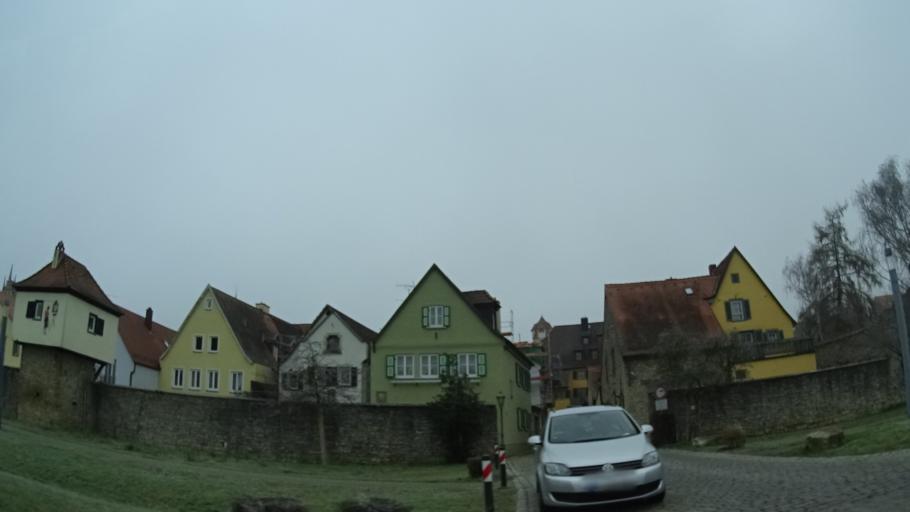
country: DE
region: Bavaria
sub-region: Regierungsbezirk Unterfranken
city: Sulzfeld am Main
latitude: 49.7085
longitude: 10.1345
